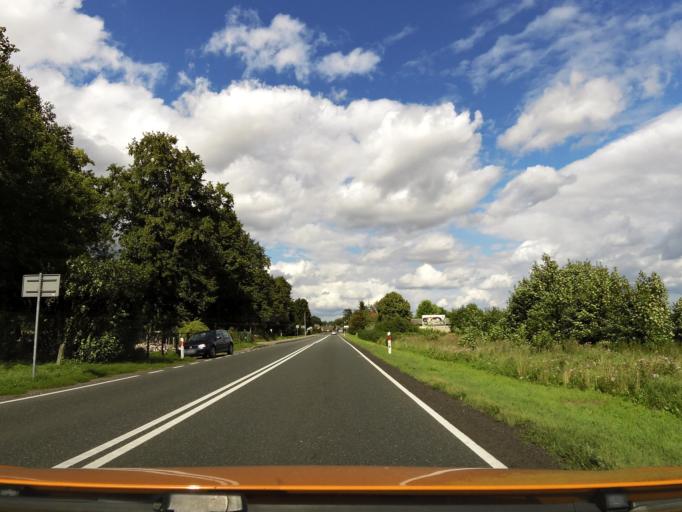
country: PL
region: West Pomeranian Voivodeship
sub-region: Powiat goleniowski
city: Nowogard
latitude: 53.7152
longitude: 15.1864
